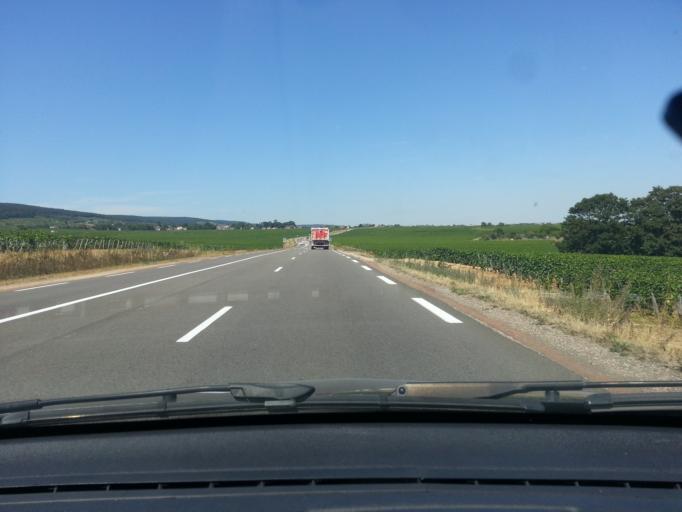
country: FR
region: Bourgogne
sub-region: Departement de la Cote-d'Or
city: Gevrey-Chambertin
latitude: 47.2085
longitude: 4.9718
